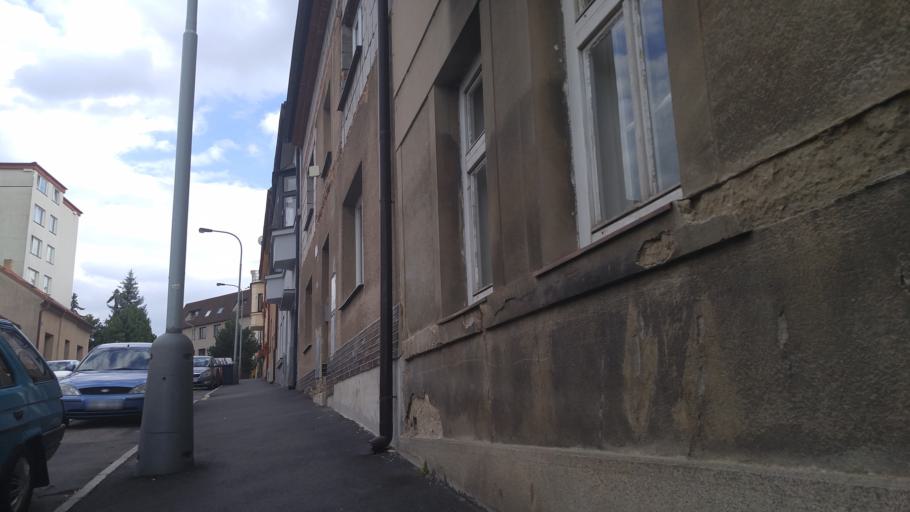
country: CZ
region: Central Bohemia
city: Horomerice
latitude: 50.0973
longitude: 14.3440
